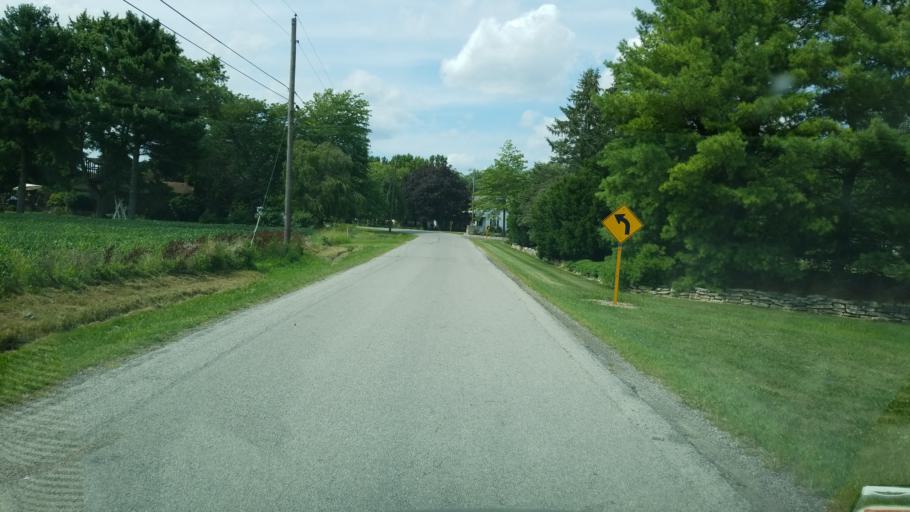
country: US
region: Ohio
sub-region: Marion County
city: Marion
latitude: 40.5300
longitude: -83.0928
